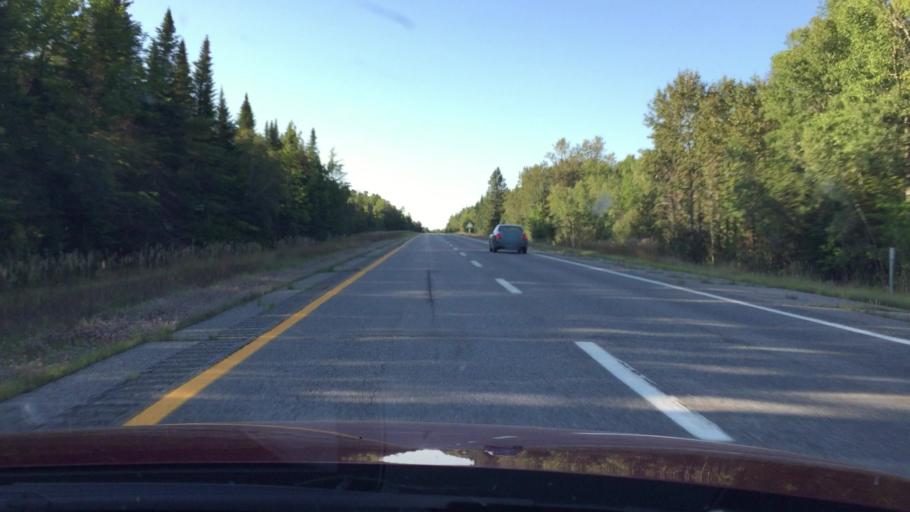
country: US
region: Maine
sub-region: Penobscot County
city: Patten
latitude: 45.8281
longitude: -68.4316
